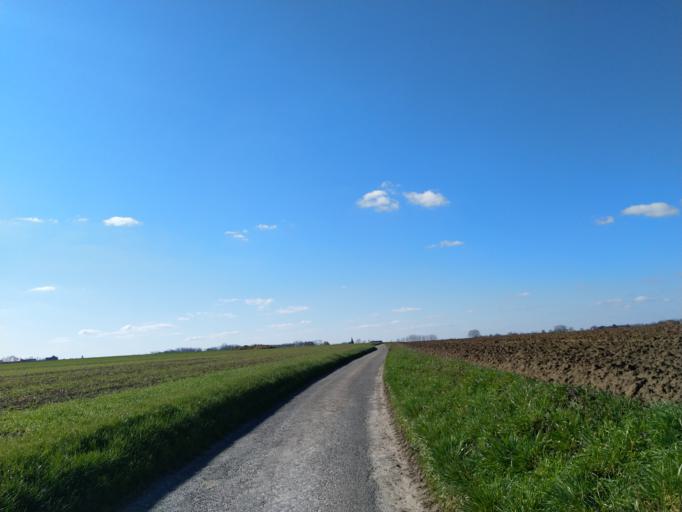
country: BE
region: Wallonia
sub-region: Province du Hainaut
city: Soignies
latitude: 50.5918
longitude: 4.0186
